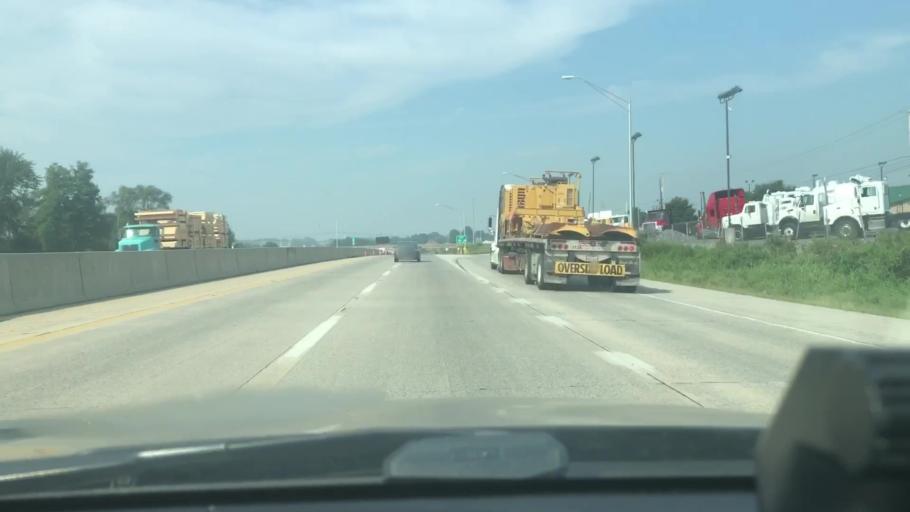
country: US
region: Pennsylvania
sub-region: Schuylkill County
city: Pine Grove
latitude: 40.4667
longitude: -76.3354
